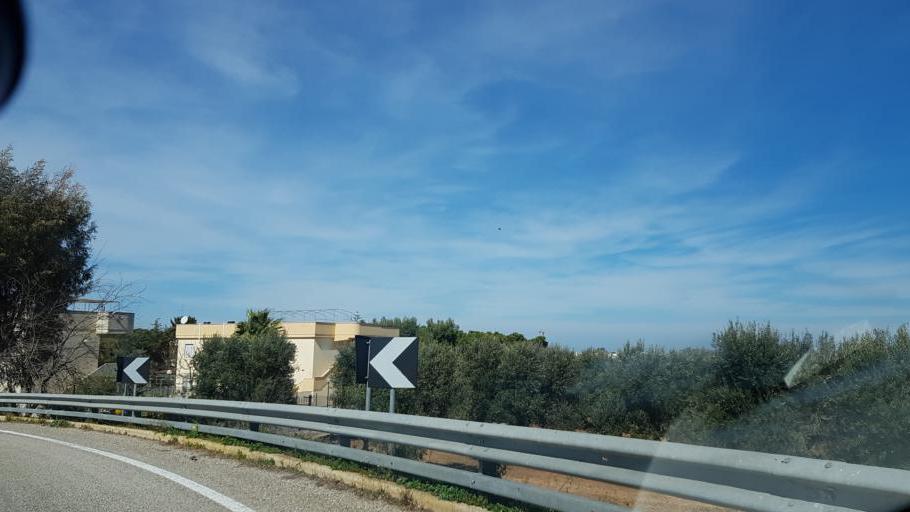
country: IT
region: Apulia
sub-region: Provincia di Brindisi
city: Pezze di Greco
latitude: 40.8314
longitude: 17.4637
